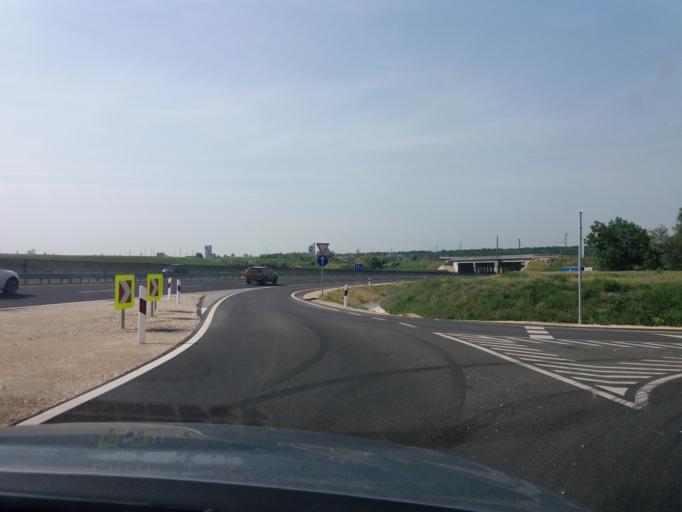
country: HU
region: Veszprem
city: Varpalota
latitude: 47.1853
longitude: 18.1360
